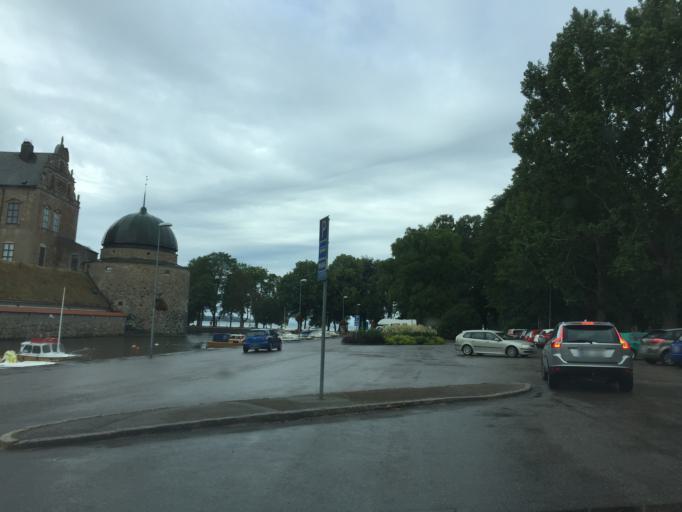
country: SE
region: OEstergoetland
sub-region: Vadstena Kommun
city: Vadstena
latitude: 58.4459
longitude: 14.8859
